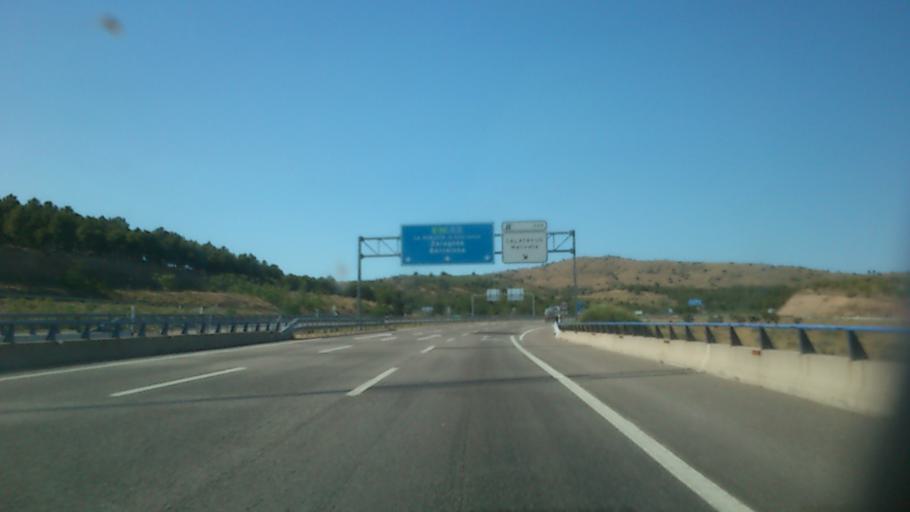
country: ES
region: Aragon
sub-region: Provincia de Zaragoza
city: Paracuellos de la Ribera
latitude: 41.3788
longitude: -1.5718
